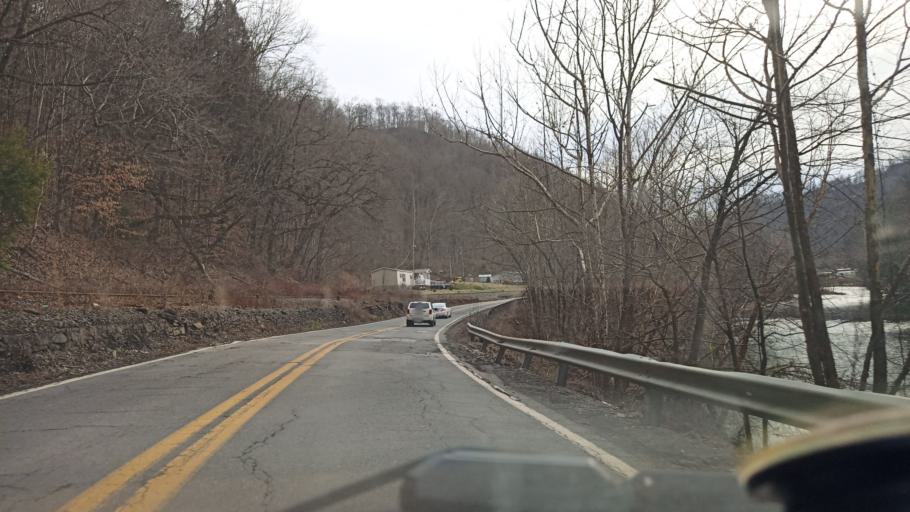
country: US
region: West Virginia
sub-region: Mingo County
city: Gilbert Creek
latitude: 37.6341
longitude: -81.8701
